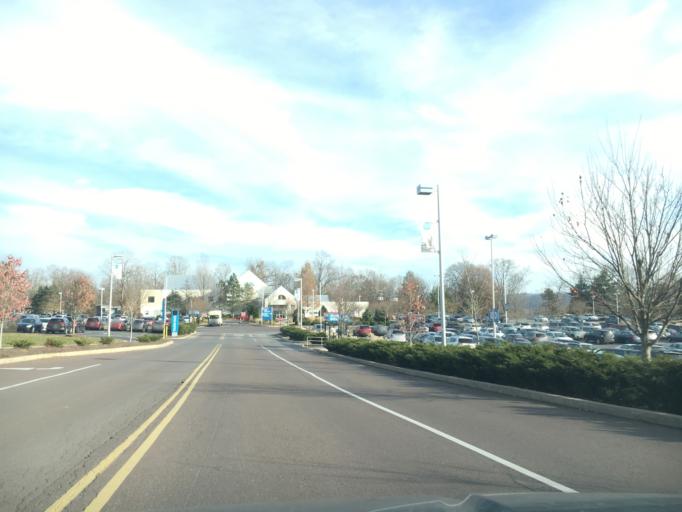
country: US
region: Pennsylvania
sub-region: Montour County
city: Danville
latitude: 40.9684
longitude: -76.6027
